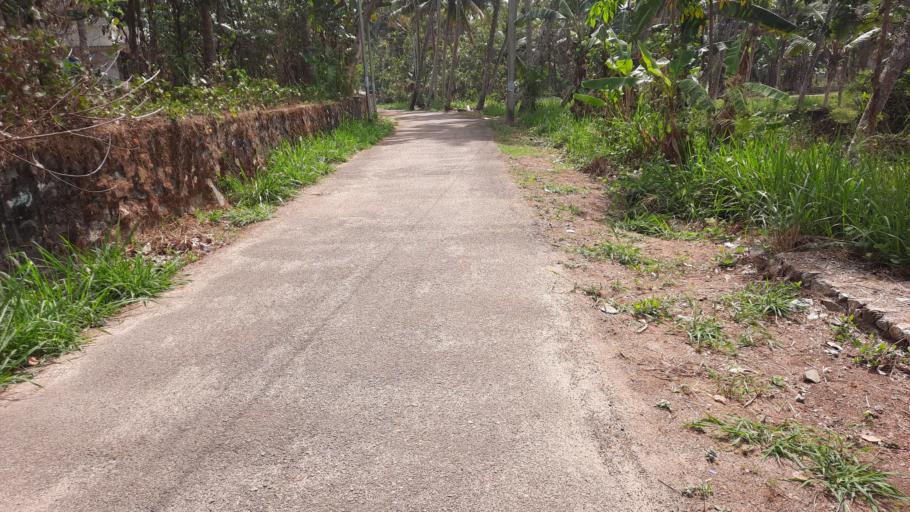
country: IN
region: Kerala
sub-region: Thiruvananthapuram
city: Thiruvananthapuram
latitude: 8.5586
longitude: 76.9299
